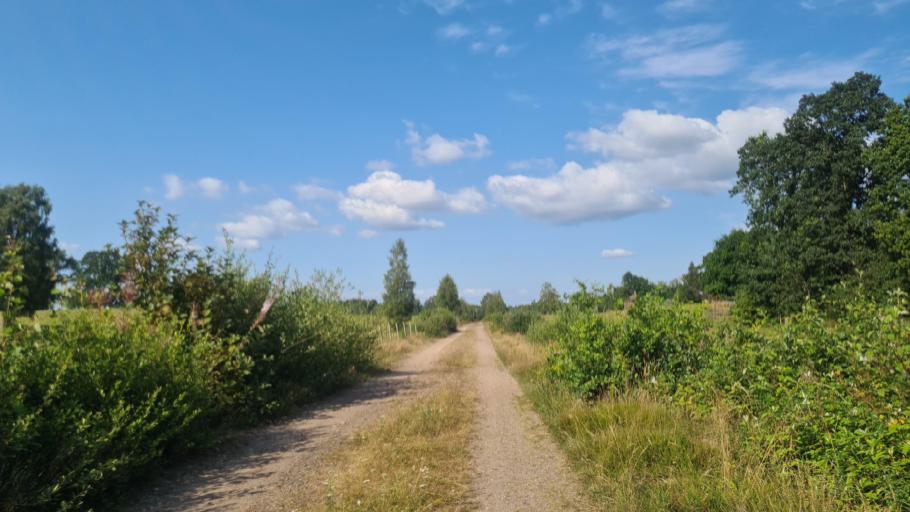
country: SE
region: Kronoberg
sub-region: Ljungby Kommun
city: Ljungby
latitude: 56.7738
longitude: 13.9001
